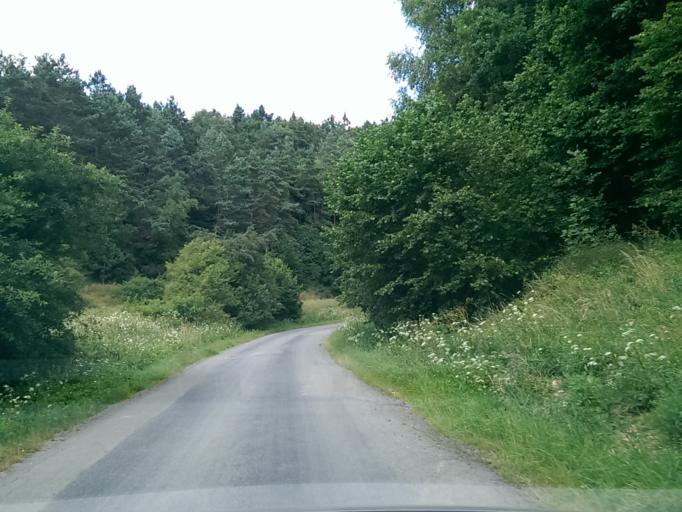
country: CZ
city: Duba
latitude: 50.4724
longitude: 14.5338
